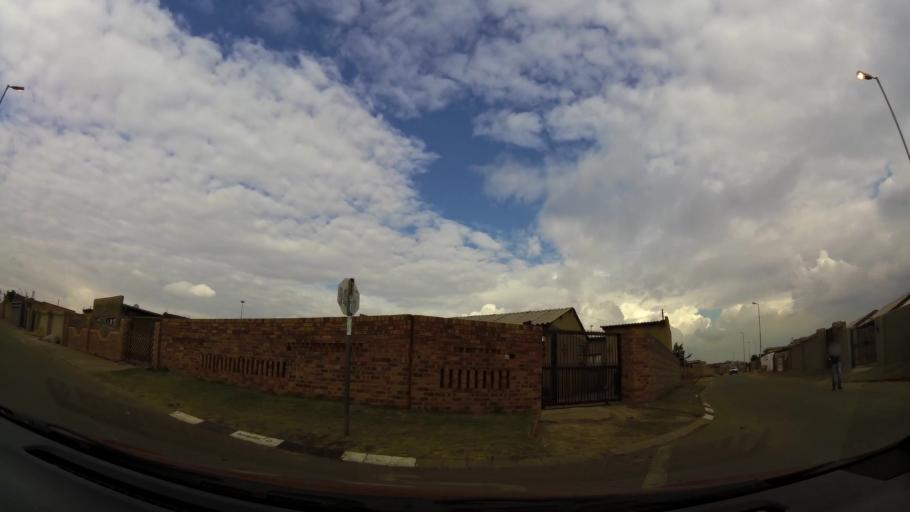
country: ZA
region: Gauteng
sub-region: City of Johannesburg Metropolitan Municipality
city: Soweto
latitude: -26.2445
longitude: 27.8513
